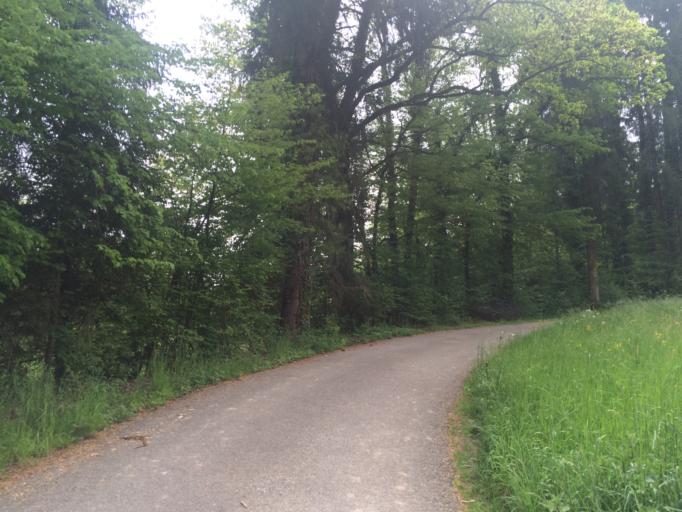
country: CH
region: Zurich
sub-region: Bezirk Uster
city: Uster / Ober-Uster
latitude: 47.3445
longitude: 8.7414
